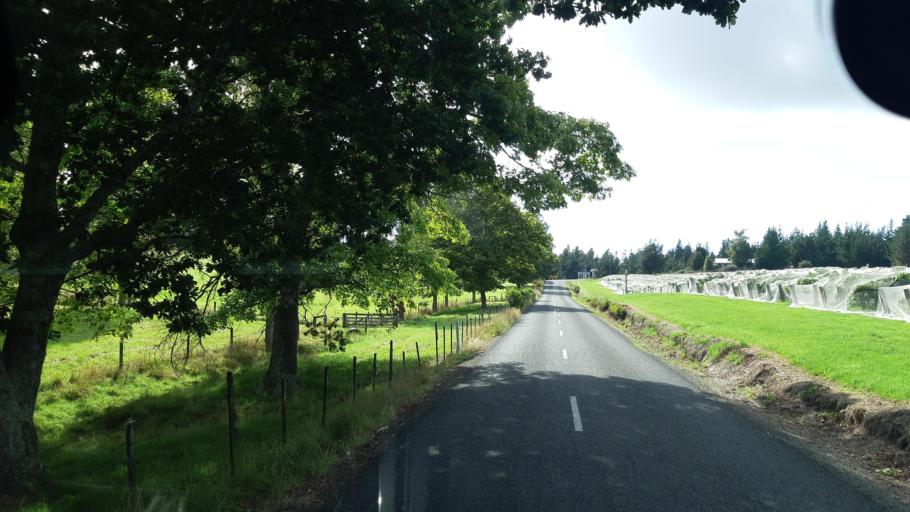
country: NZ
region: Tasman
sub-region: Tasman District
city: Mapua
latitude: -41.2593
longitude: 173.0444
